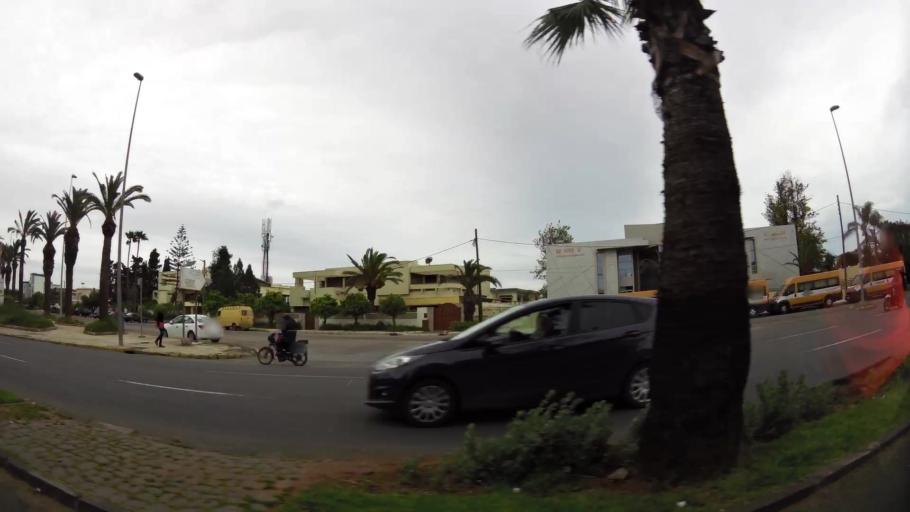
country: MA
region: Grand Casablanca
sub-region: Casablanca
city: Casablanca
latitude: 33.5619
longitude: -7.6226
